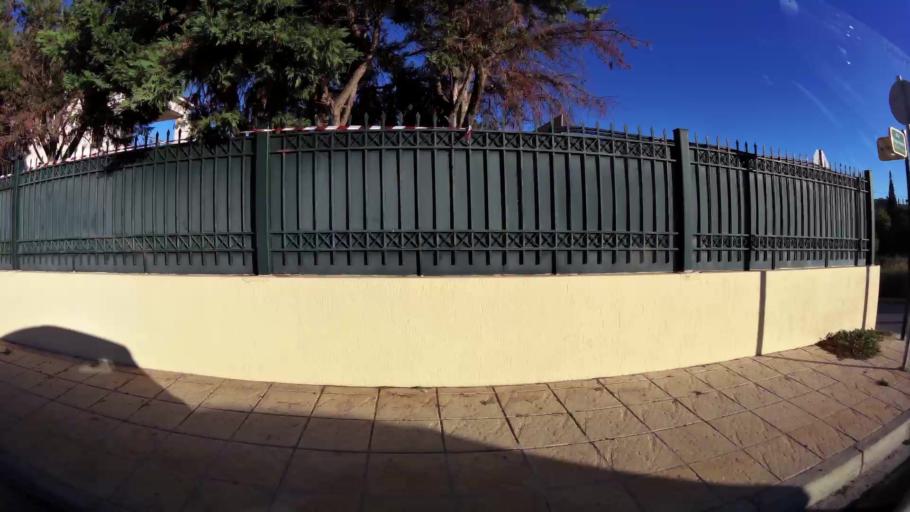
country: GR
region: Attica
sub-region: Nomarchia Anatolikis Attikis
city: Vari
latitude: 37.8236
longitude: 23.8005
